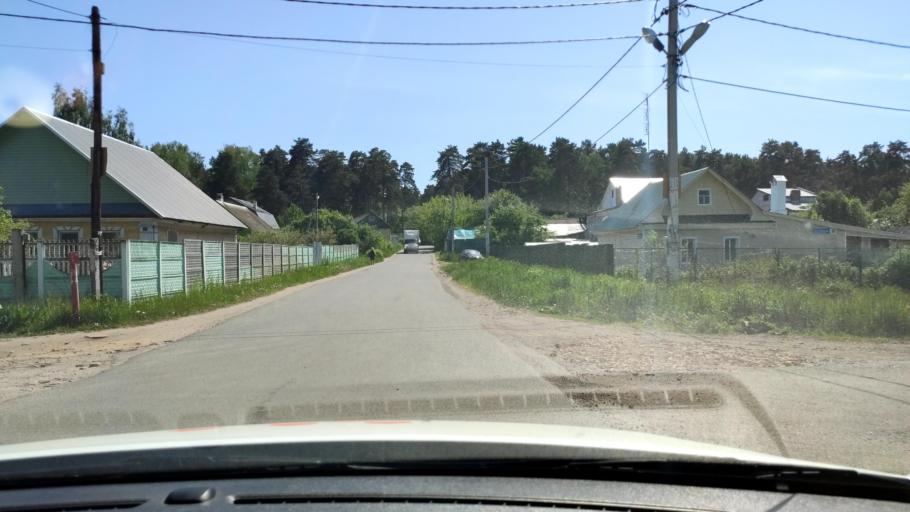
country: RU
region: Tatarstan
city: Osinovo
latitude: 55.8260
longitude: 48.8725
